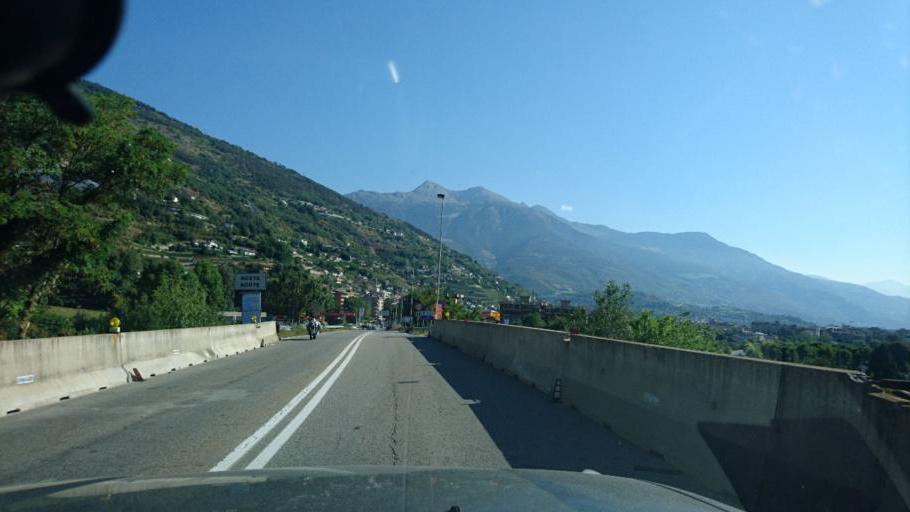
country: IT
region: Aosta Valley
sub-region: Valle d'Aosta
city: Gressan
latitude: 45.7302
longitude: 7.2888
